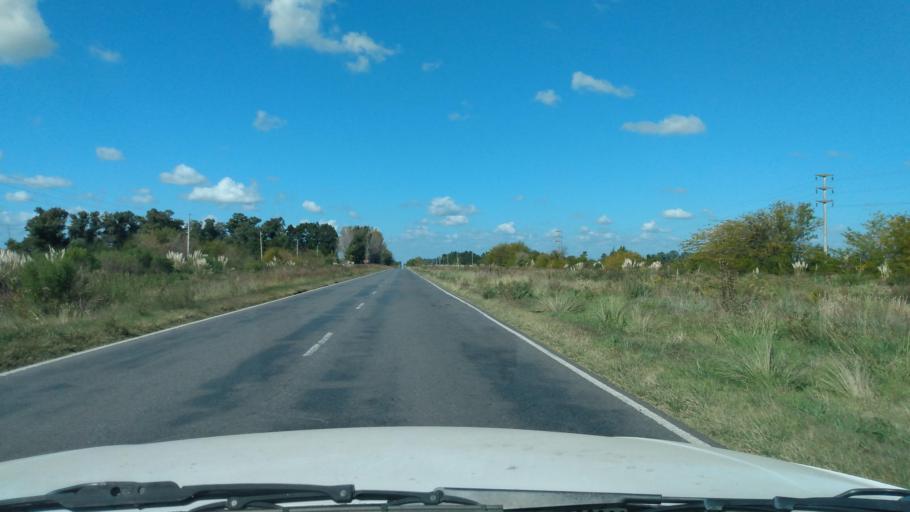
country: AR
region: Buenos Aires
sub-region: Partido de Mercedes
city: Mercedes
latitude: -34.7117
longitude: -59.3988
